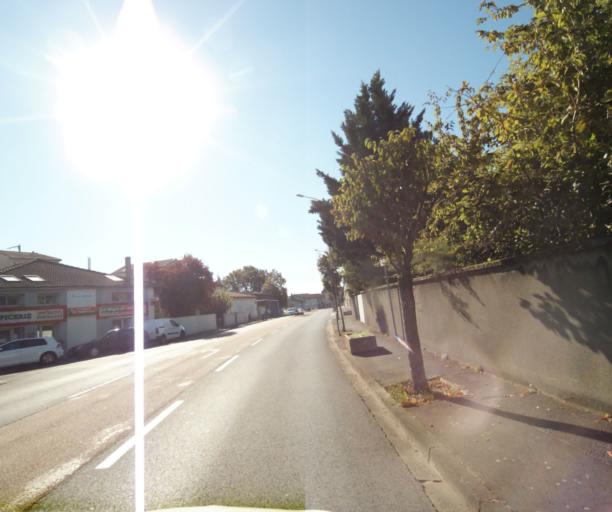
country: FR
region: Auvergne
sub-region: Departement du Puy-de-Dome
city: Gerzat
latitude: 45.8247
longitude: 3.1417
